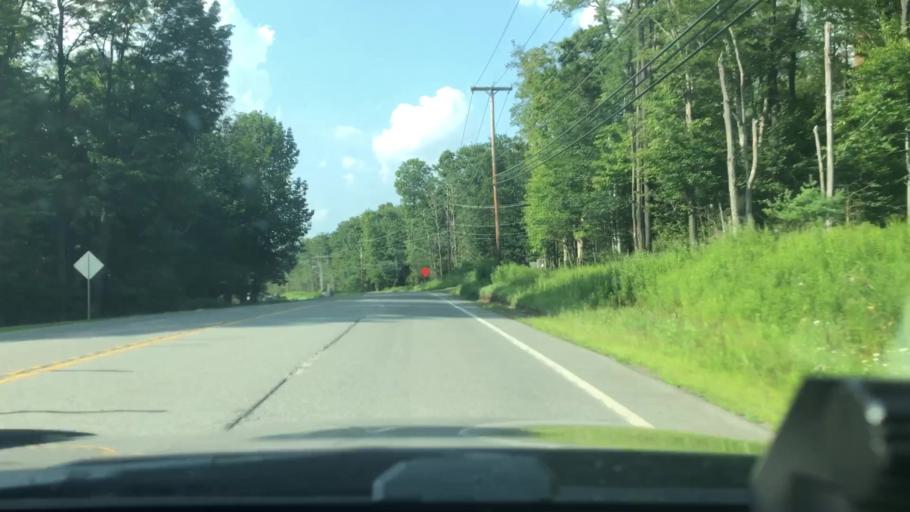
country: US
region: Pennsylvania
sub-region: Lackawanna County
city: Moscow
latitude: 41.2738
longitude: -75.5063
